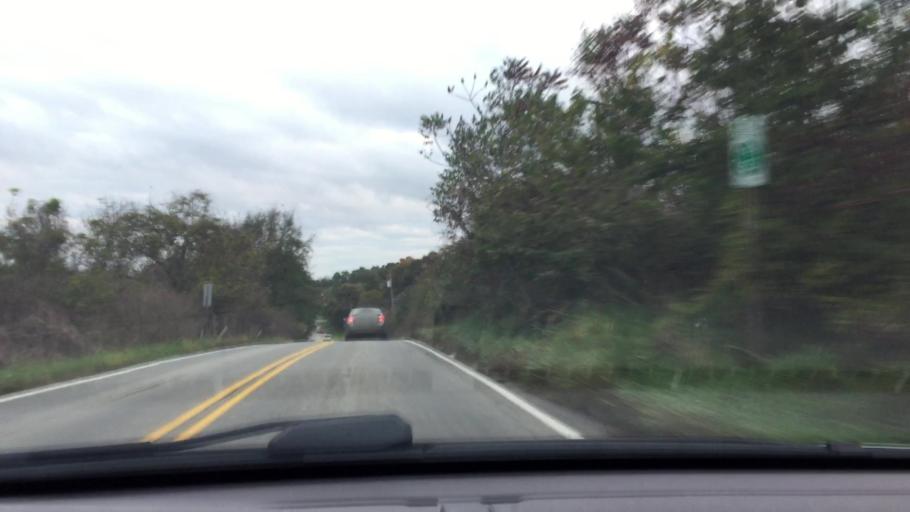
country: US
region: Pennsylvania
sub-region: Washington County
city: McMurray
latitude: 40.1985
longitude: -80.1196
